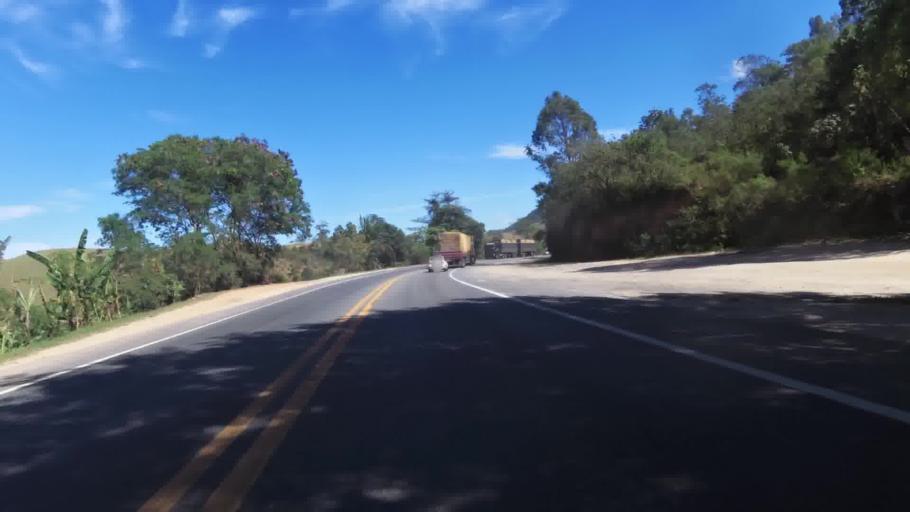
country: BR
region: Espirito Santo
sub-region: Rio Novo Do Sul
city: Rio Novo do Sul
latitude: -20.8669
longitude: -40.8946
